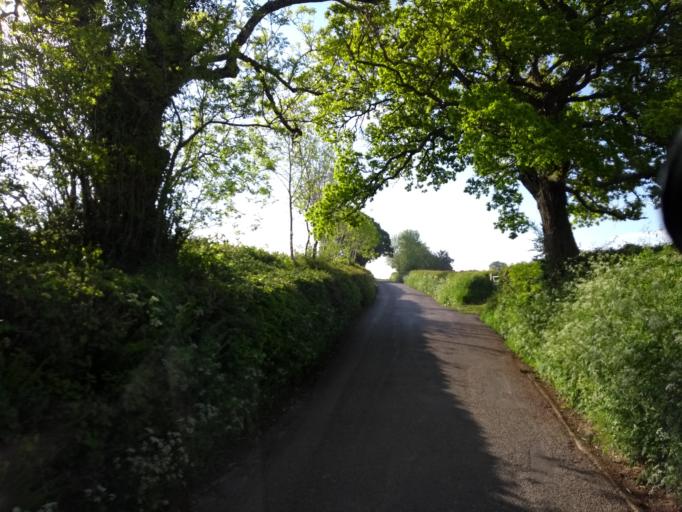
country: GB
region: England
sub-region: Devon
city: Axminster
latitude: 50.7974
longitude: -2.9297
